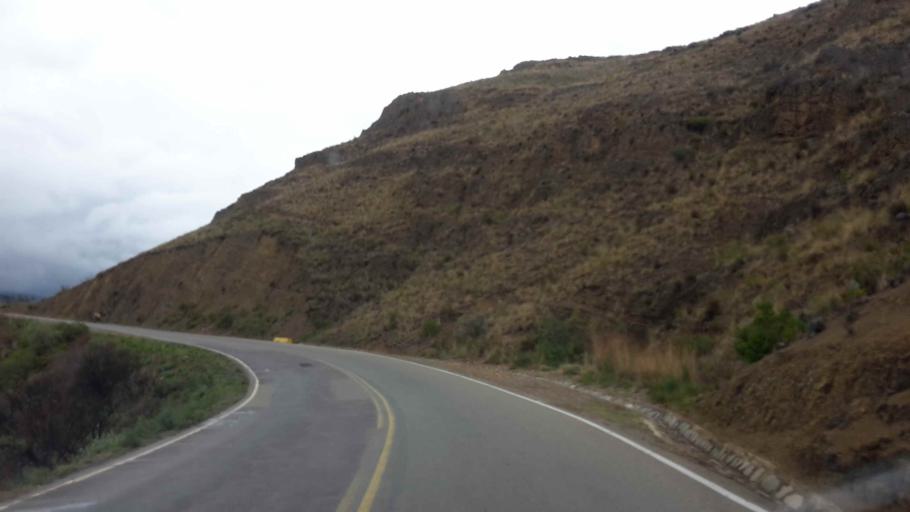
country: BO
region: Cochabamba
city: Punata
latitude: -17.4837
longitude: -65.7784
